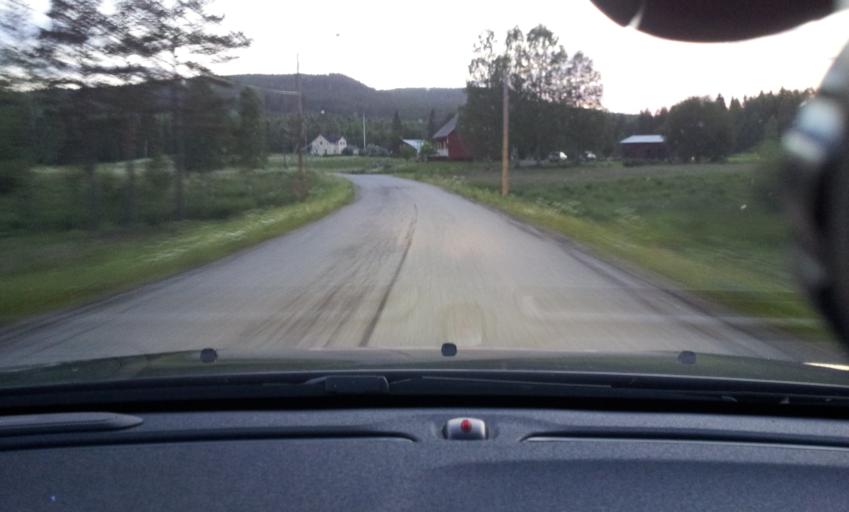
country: SE
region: Vaesternorrland
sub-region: Ange Kommun
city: Fransta
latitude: 62.7818
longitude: 16.0010
